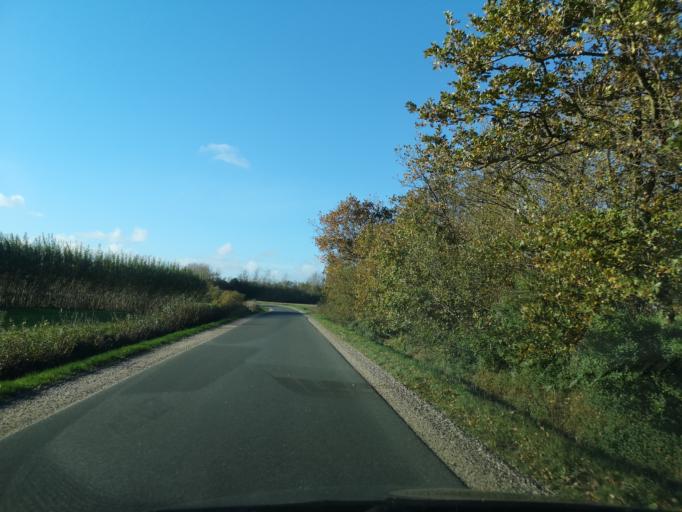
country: DK
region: Central Jutland
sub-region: Ringkobing-Skjern Kommune
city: Tarm
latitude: 55.8158
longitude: 8.4279
